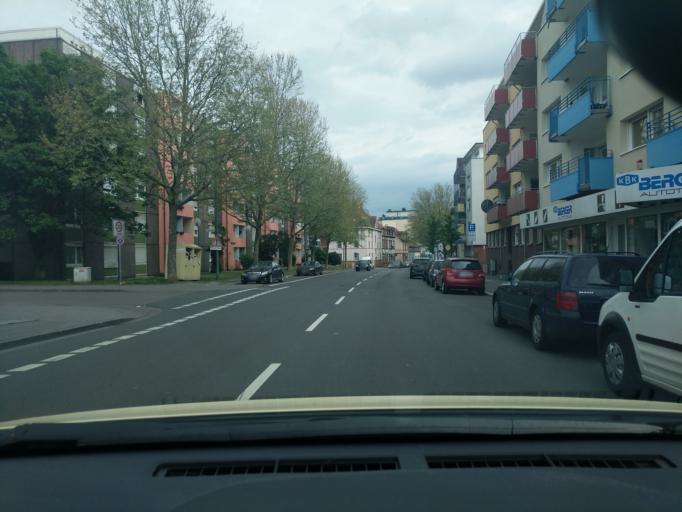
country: DE
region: Rheinland-Pfalz
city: Kaiserslautern
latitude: 49.4492
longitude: 7.7811
